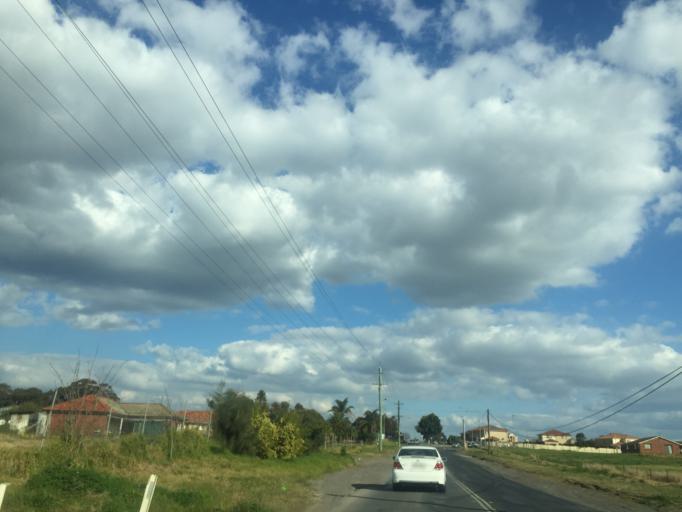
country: AU
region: New South Wales
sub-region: Blacktown
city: Quakers Hill
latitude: -33.7110
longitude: 150.8934
